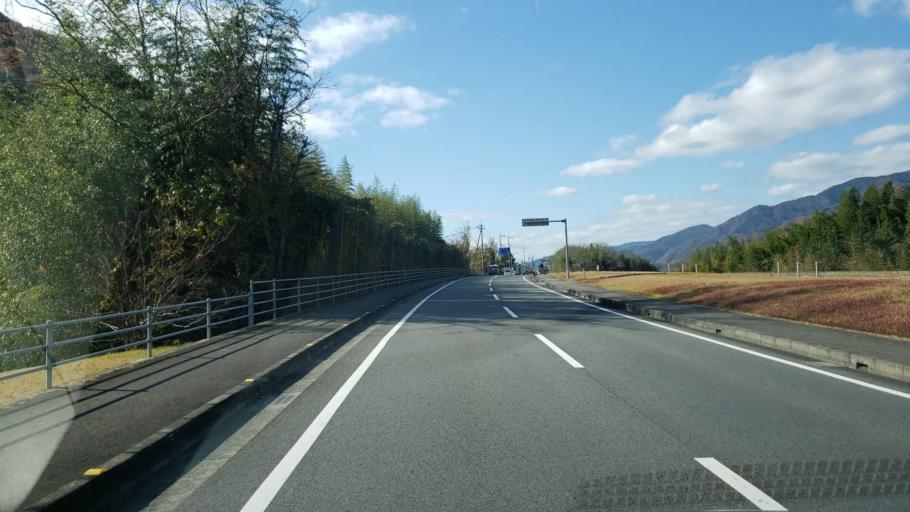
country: JP
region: Tokushima
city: Wakimachi
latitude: 34.0422
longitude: 134.0541
